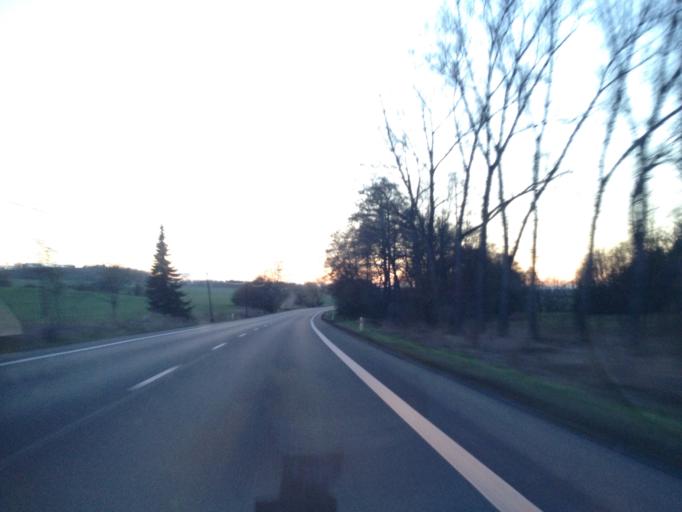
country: CZ
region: Central Bohemia
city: Jesenice
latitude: 50.1378
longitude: 13.4571
